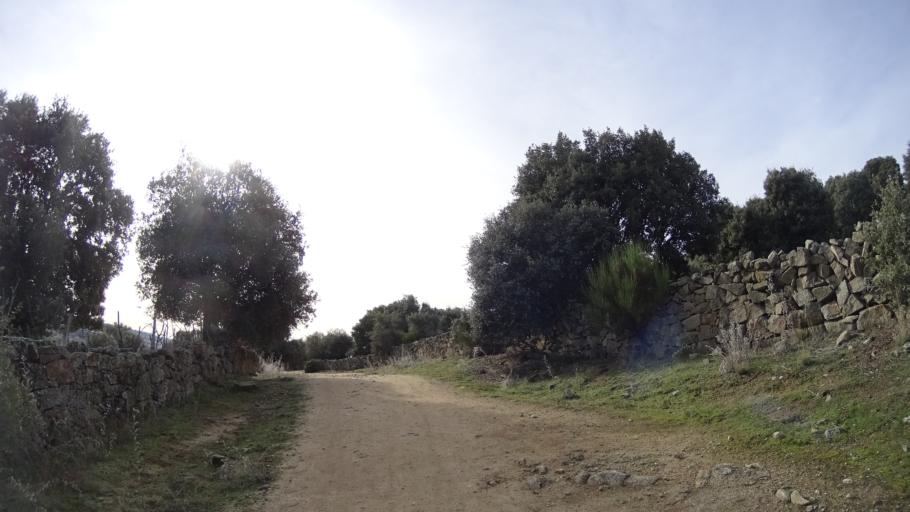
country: ES
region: Madrid
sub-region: Provincia de Madrid
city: Moralzarzal
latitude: 40.6637
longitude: -3.9949
